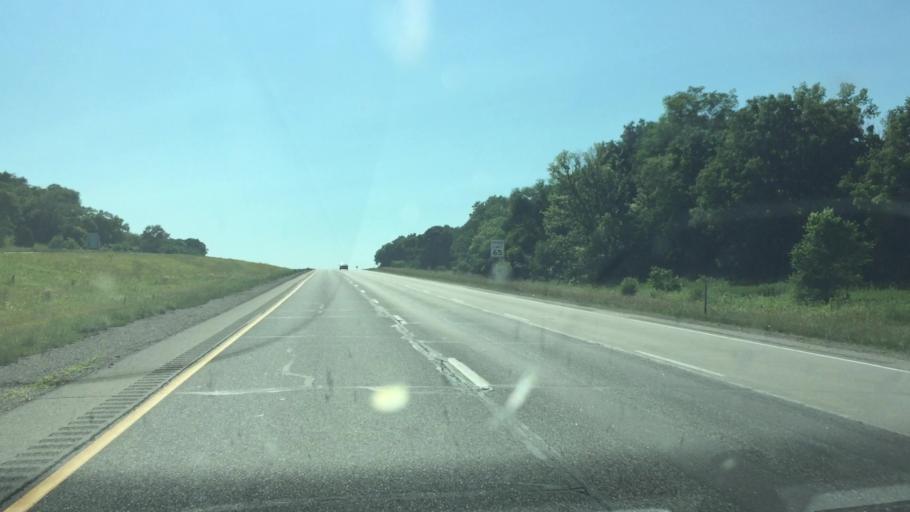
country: US
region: Iowa
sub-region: Linn County
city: Ely
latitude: 41.9259
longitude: -91.5576
